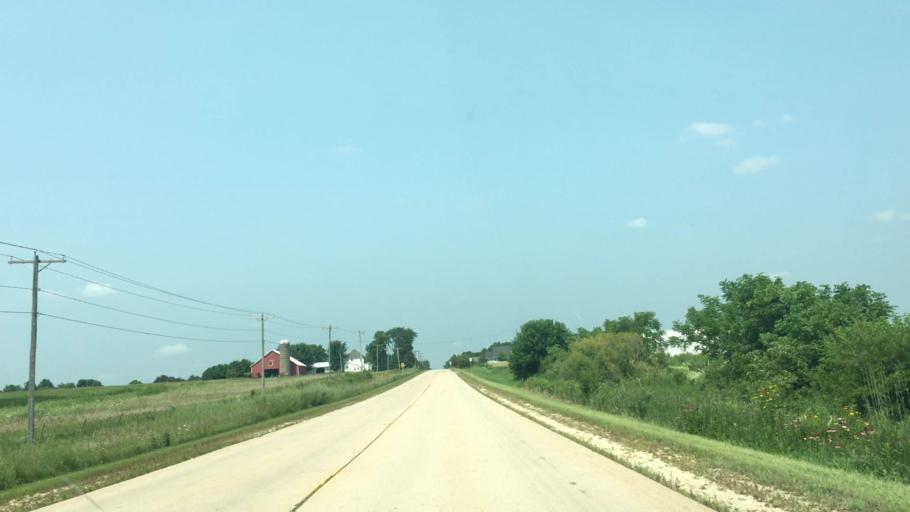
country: US
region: Iowa
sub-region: Fayette County
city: Oelwein
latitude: 42.6708
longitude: -91.8938
